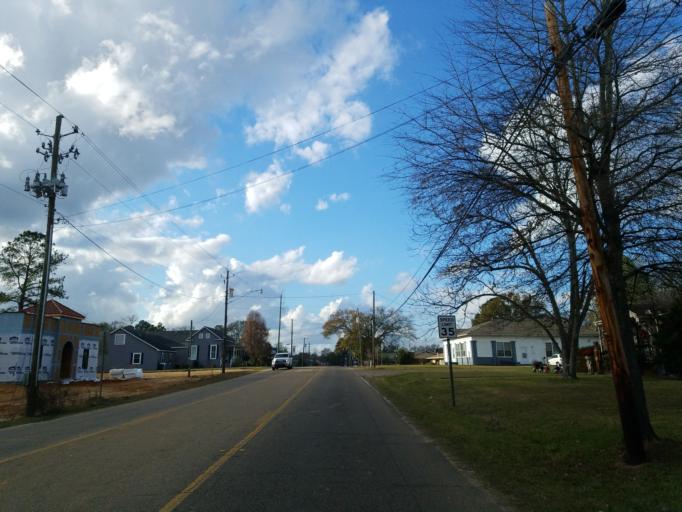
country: US
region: Mississippi
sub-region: Jones County
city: Ellisville
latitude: 31.6074
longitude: -89.2001
